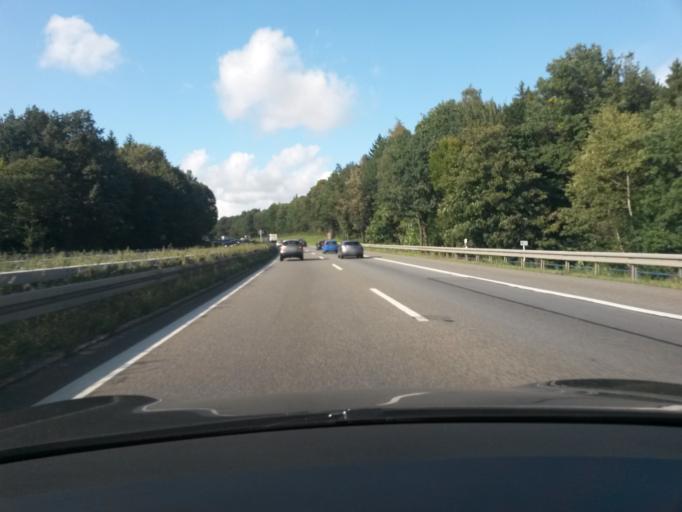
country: DE
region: Bavaria
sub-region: Upper Palatinate
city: Sinzing
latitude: 48.9993
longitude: 12.0041
